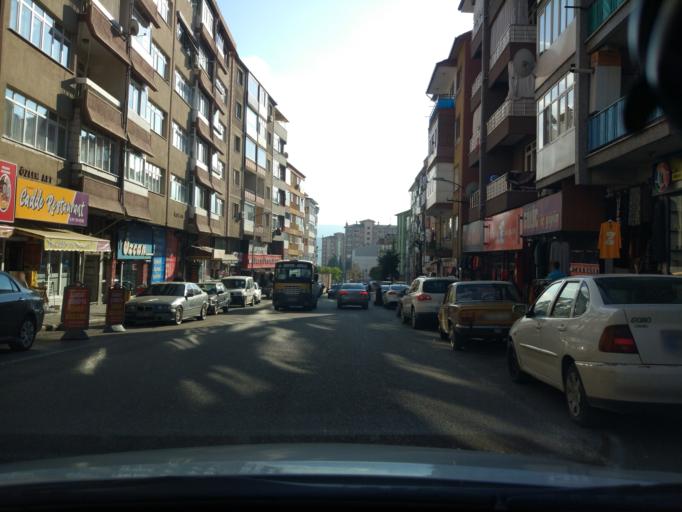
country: TR
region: Karabuk
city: Karabuk
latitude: 41.2058
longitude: 32.6266
